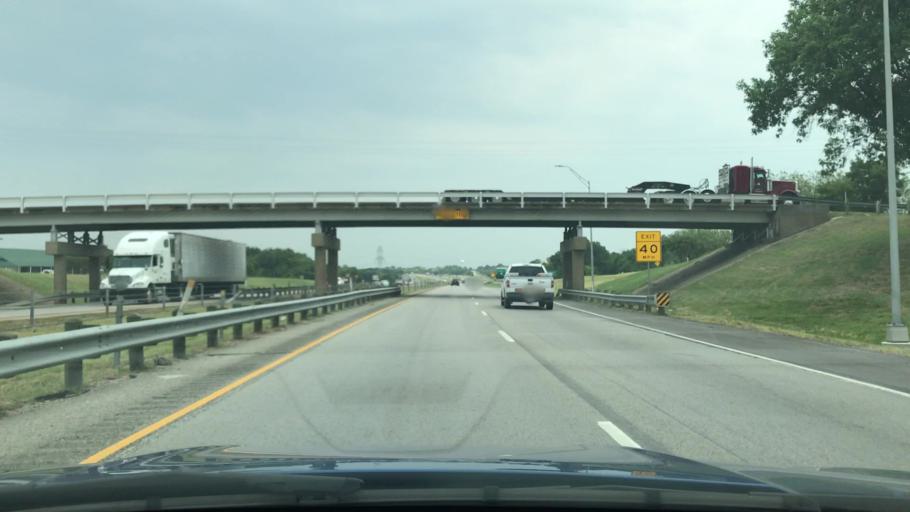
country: US
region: Texas
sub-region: Kaufman County
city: Forney
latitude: 32.7701
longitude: -96.4891
